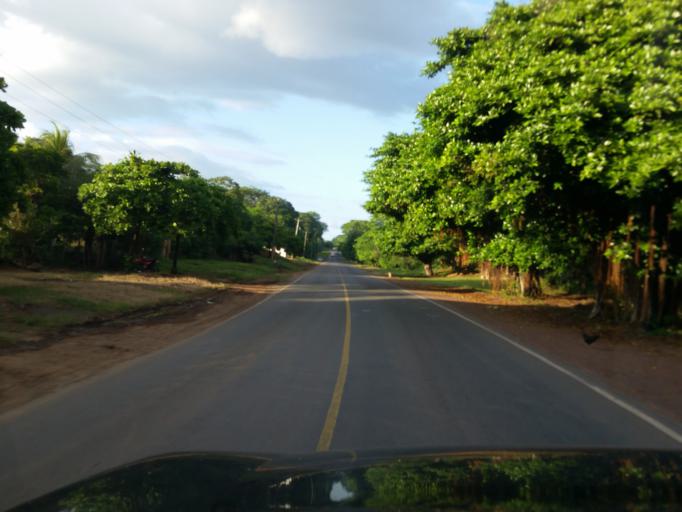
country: NI
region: Granada
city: Nandaime
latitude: 11.7799
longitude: -86.0501
